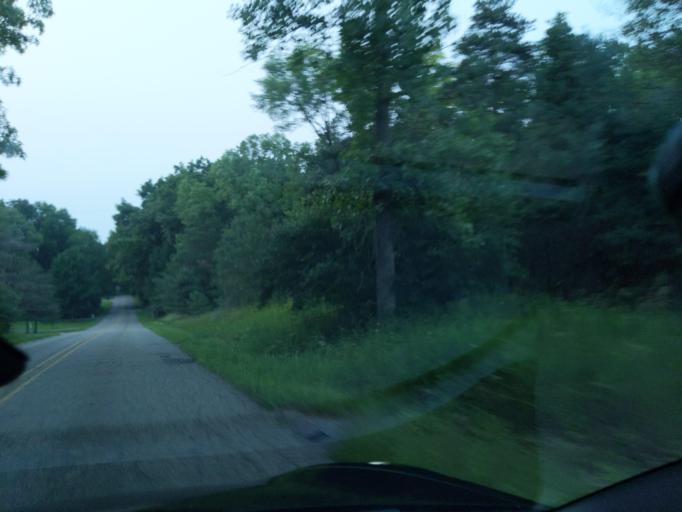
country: US
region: Michigan
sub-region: Ingham County
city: Leslie
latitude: 42.3591
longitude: -84.4924
